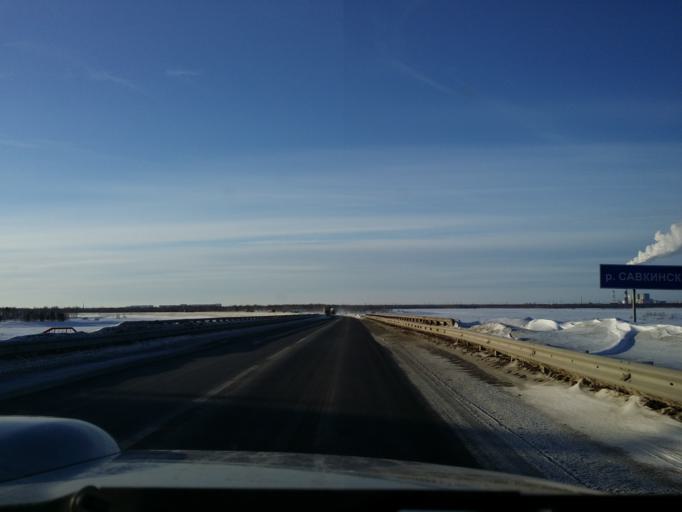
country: RU
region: Khanty-Mansiyskiy Avtonomnyy Okrug
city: Izluchinsk
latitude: 60.9339
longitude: 76.9823
